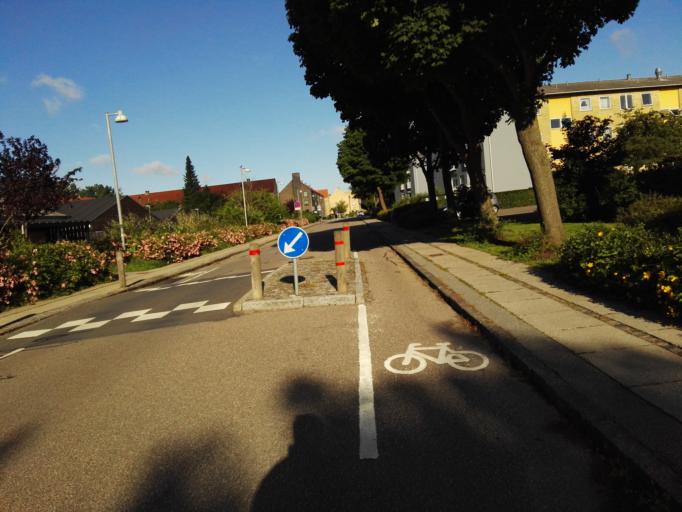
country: DK
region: Capital Region
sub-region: Ballerup Kommune
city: Ballerup
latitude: 55.7242
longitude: 12.3646
